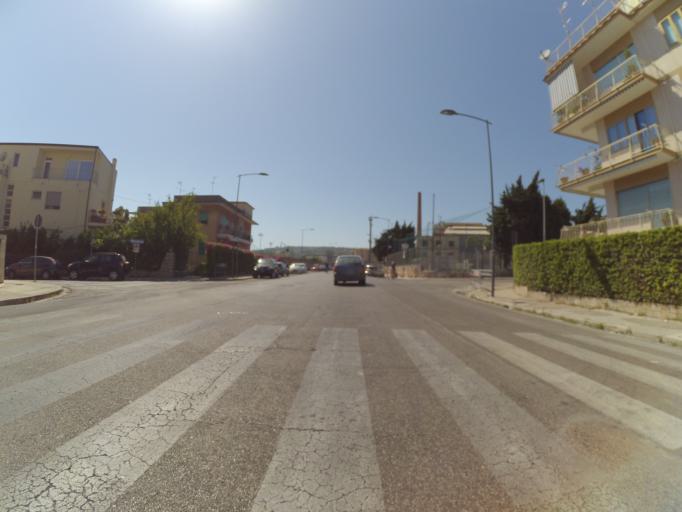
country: IT
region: Latium
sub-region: Provincia di Latina
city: Gaeta
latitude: 41.2113
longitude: 13.5686
